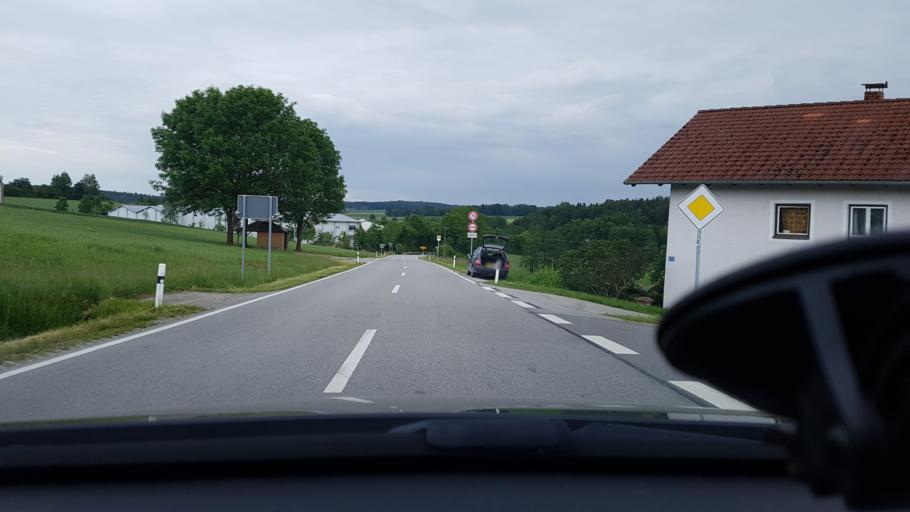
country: DE
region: Bavaria
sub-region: Lower Bavaria
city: Triftern
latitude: 48.3601
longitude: 13.0075
